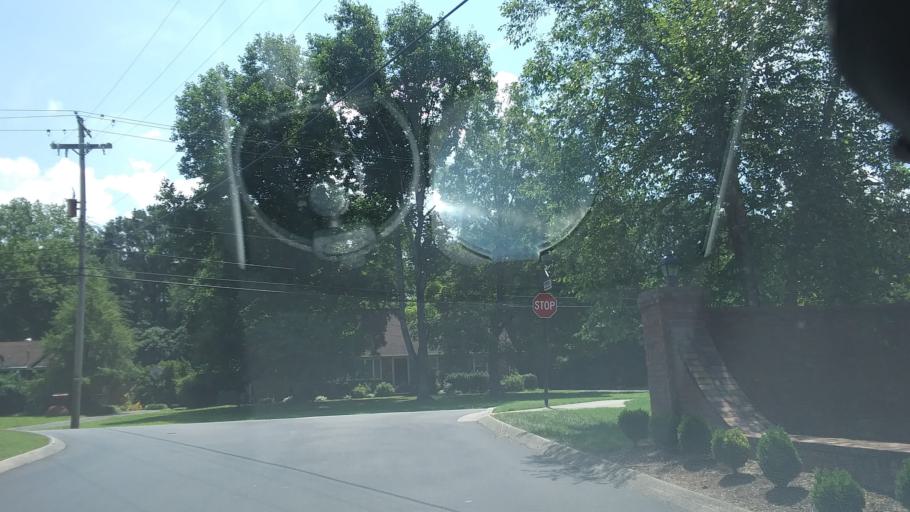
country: US
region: Tennessee
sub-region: Davidson County
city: Belle Meade
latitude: 36.0843
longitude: -86.9442
